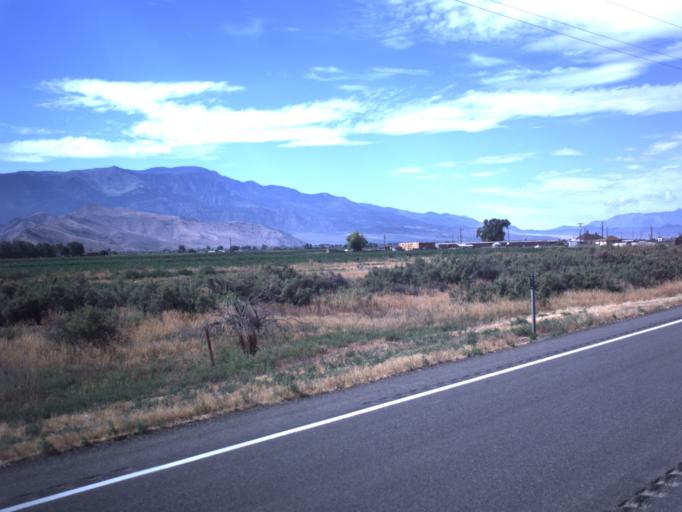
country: US
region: Utah
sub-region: Sevier County
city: Richfield
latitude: 38.8056
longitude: -112.0235
